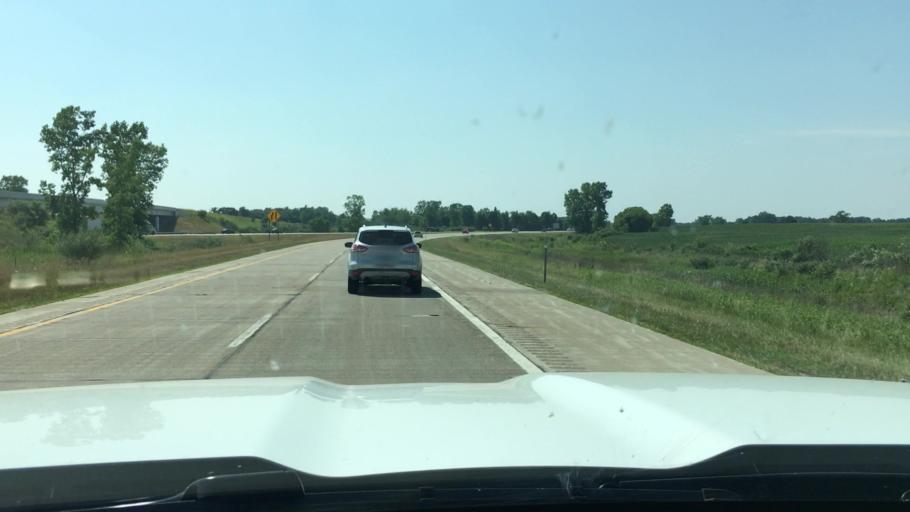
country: US
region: Michigan
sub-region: Clinton County
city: Wacousta
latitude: 42.7897
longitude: -84.6734
